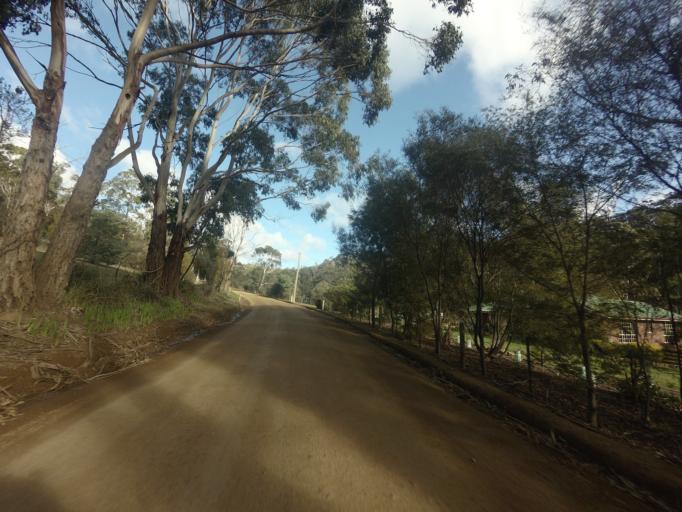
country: AU
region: Tasmania
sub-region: Derwent Valley
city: New Norfolk
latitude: -42.8099
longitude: 147.1323
